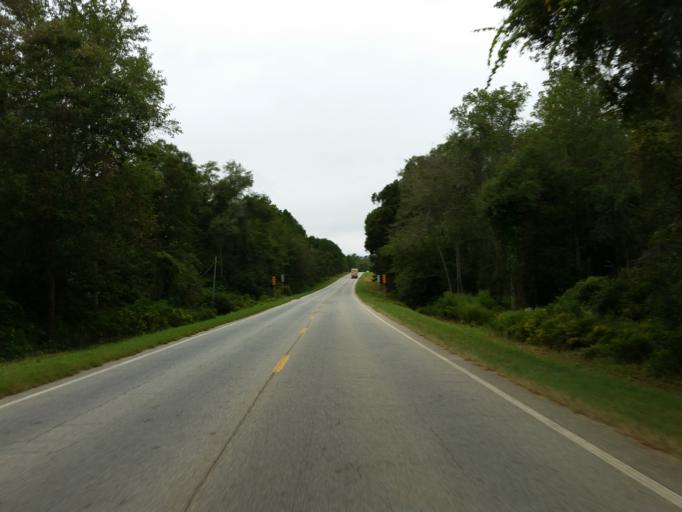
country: US
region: Georgia
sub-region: Cook County
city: Adel
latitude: 31.1315
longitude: -83.3662
